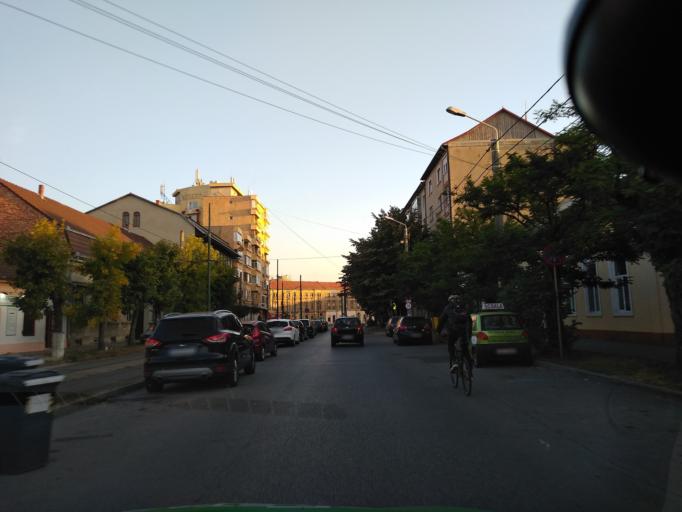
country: RO
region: Timis
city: Timisoara
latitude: 45.7401
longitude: 21.2252
